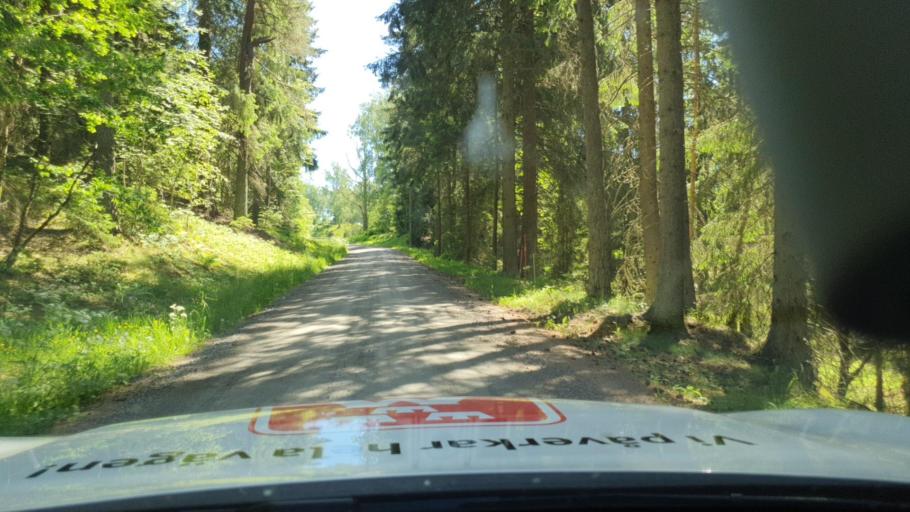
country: SE
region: Joenkoeping
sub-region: Mullsjo Kommun
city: Mullsjoe
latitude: 58.0446
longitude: 13.8751
